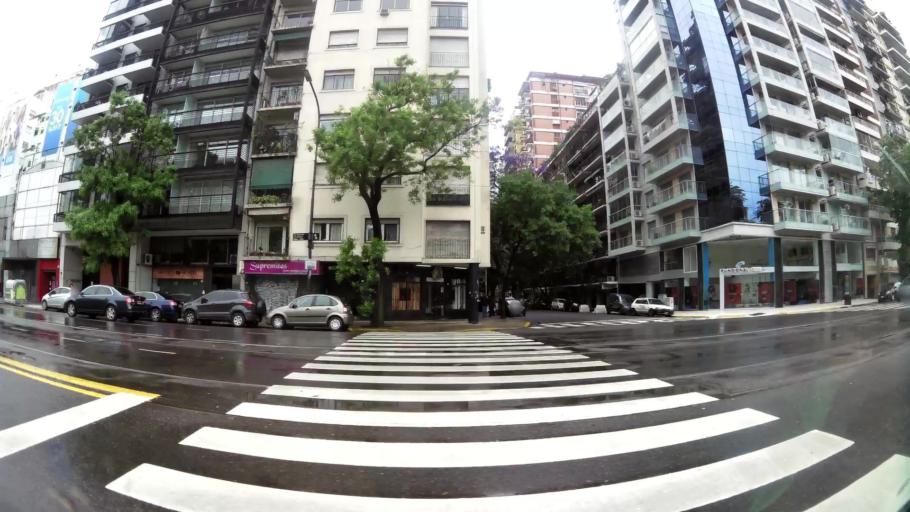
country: AR
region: Buenos Aires F.D.
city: Retiro
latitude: -34.5824
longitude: -58.4091
